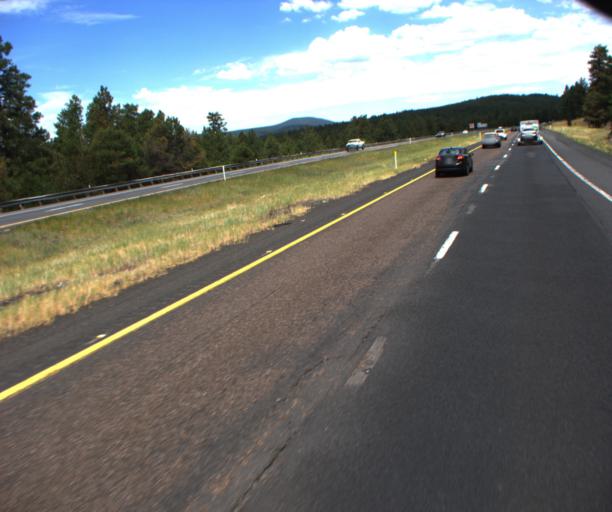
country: US
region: Arizona
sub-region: Coconino County
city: Mountainaire
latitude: 35.0583
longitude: -111.6844
